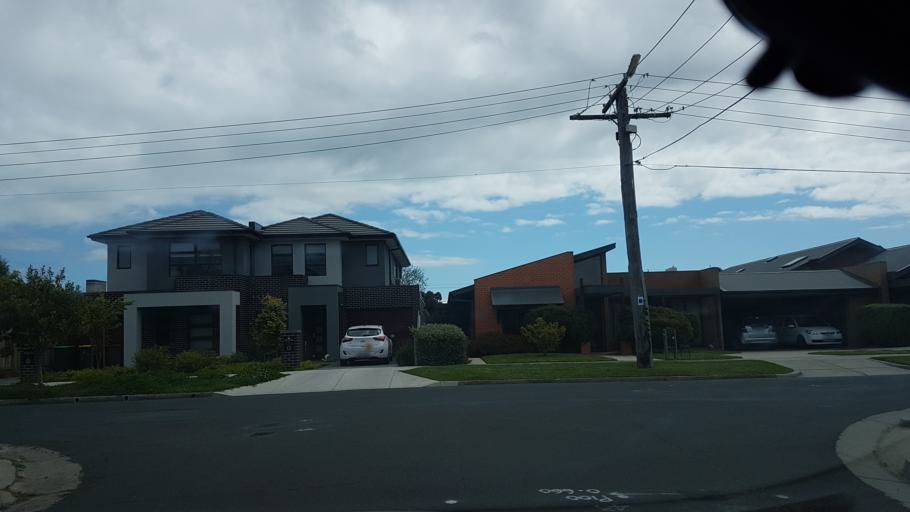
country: AU
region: Victoria
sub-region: Glen Eira
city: Bentleigh
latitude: -37.9249
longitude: 145.0418
